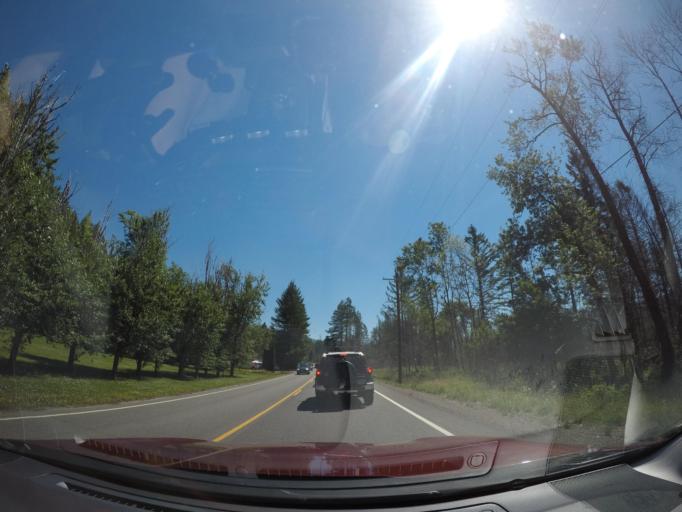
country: US
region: Oregon
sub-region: Linn County
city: Mill City
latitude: 44.7557
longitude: -122.4117
